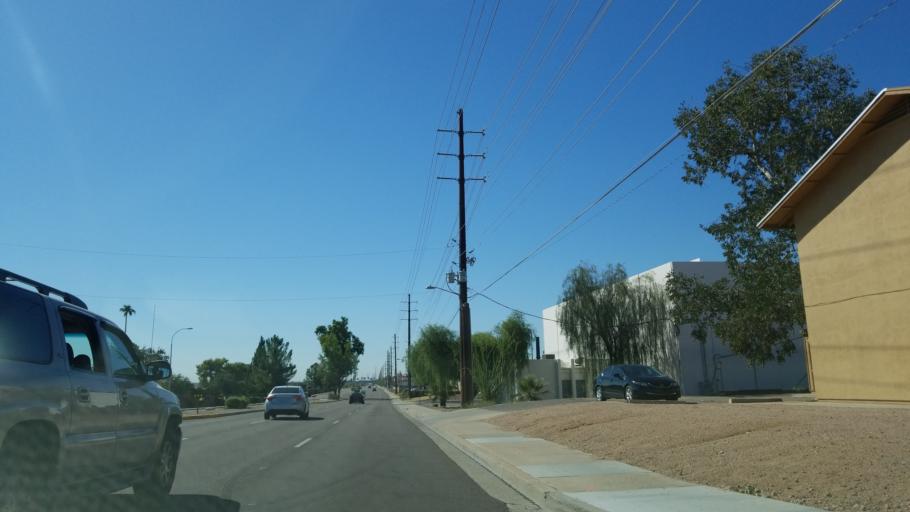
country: US
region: Arizona
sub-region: Maricopa County
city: Tempe
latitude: 33.4582
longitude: -111.9092
